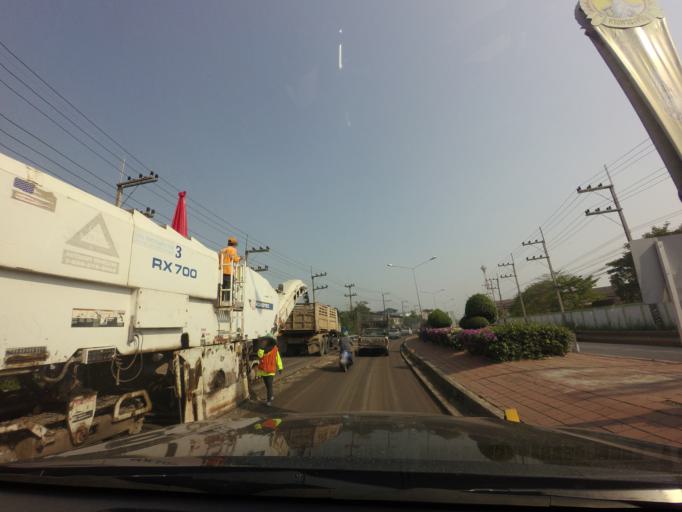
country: TH
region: Kanchanaburi
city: Tha Maka
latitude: 13.8977
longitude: 99.7942
